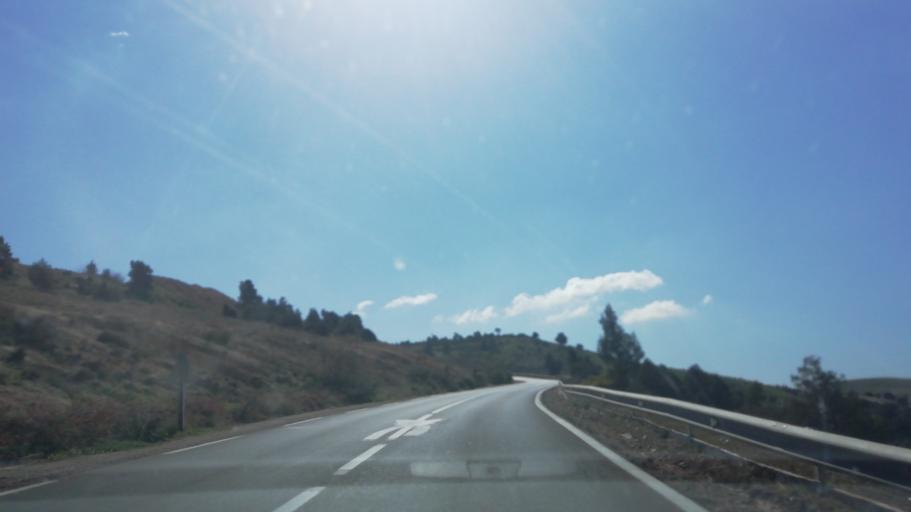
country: DZ
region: Mascara
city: Mascara
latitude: 35.4940
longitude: 0.1336
